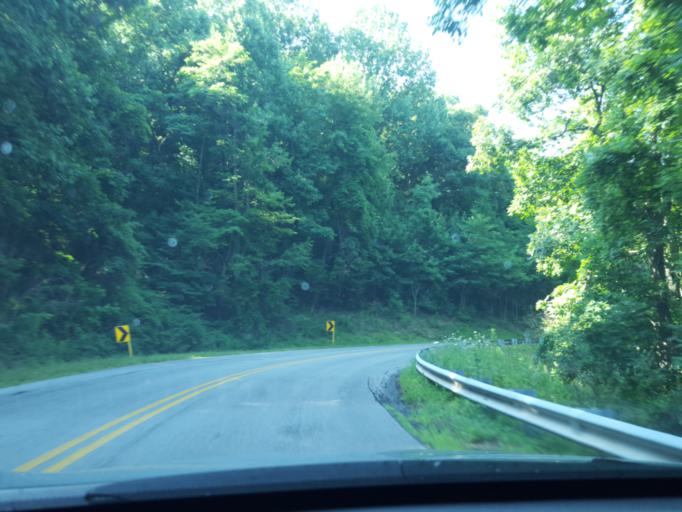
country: US
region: Virginia
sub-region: Nelson County
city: Nellysford
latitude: 37.9067
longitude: -78.9882
